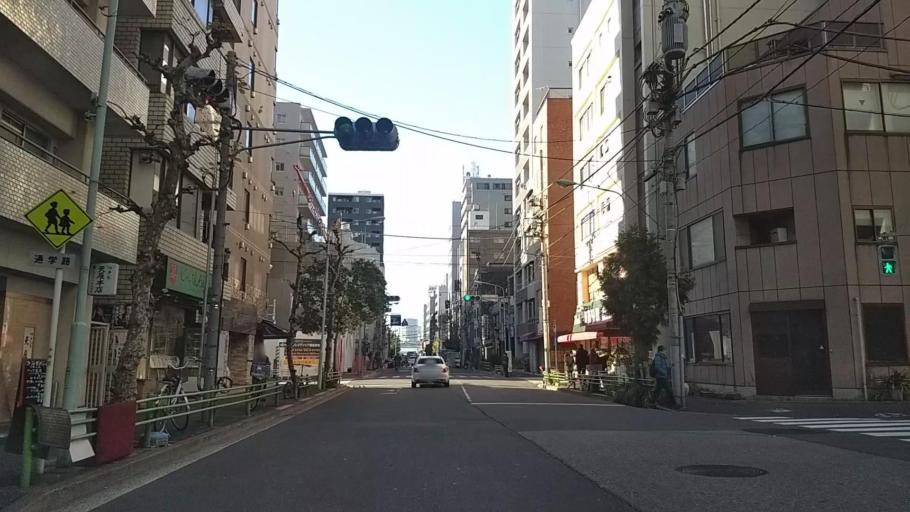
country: JP
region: Tokyo
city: Tokyo
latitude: 35.6656
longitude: 139.7743
